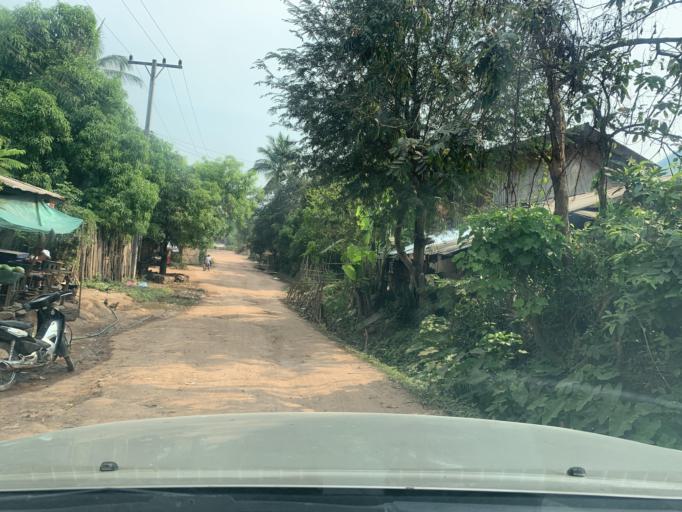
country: LA
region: Louangphabang
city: Louangphabang
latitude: 19.9120
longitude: 102.1373
